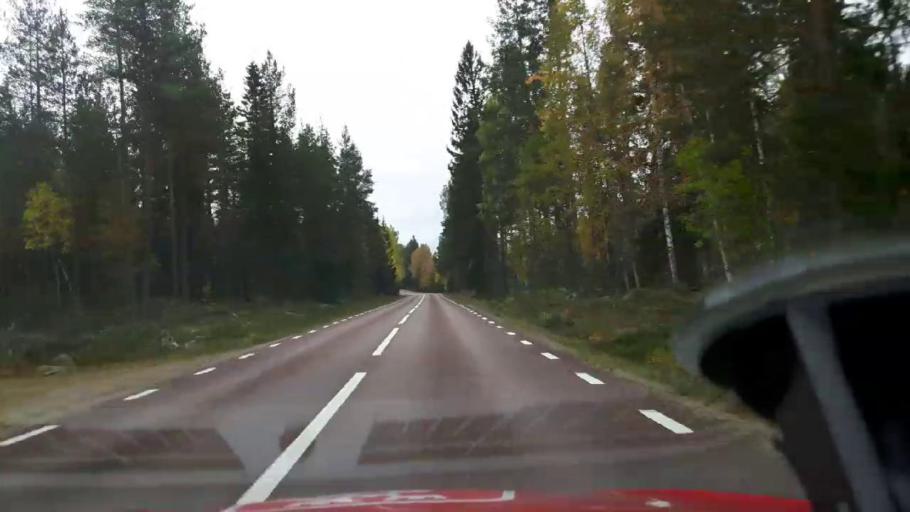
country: SE
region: Jaemtland
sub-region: Harjedalens Kommun
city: Sveg
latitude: 62.2160
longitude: 14.8463
